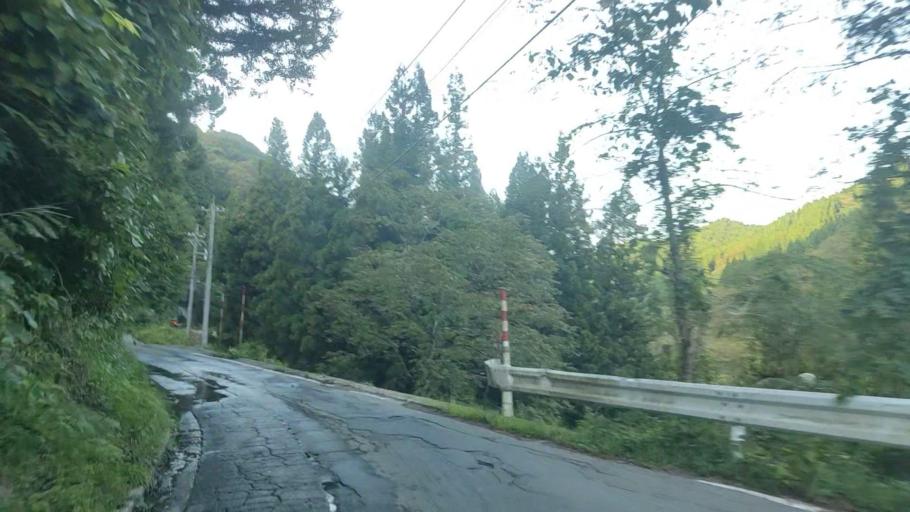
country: JP
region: Toyama
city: Yatsuomachi-higashikumisaka
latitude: 36.4960
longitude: 137.0638
